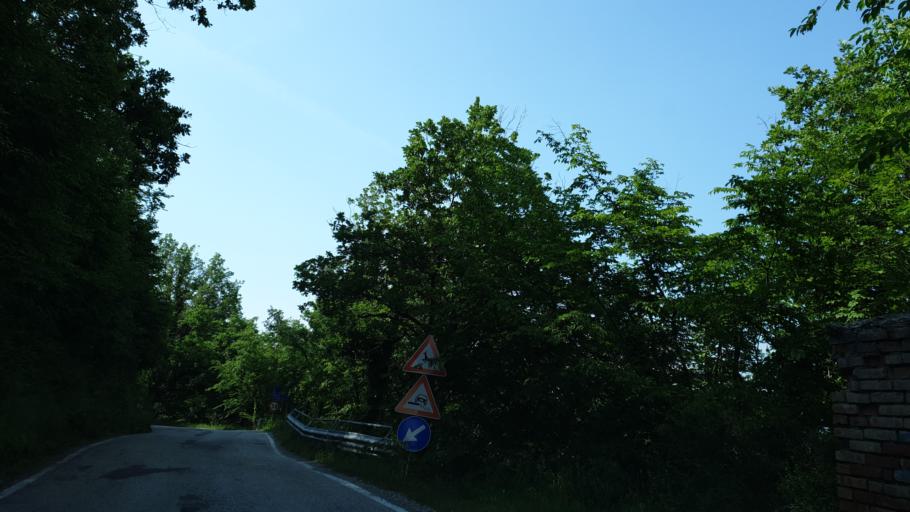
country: IT
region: Emilia-Romagna
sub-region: Forli-Cesena
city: Sarsina
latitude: 43.9088
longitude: 12.1781
